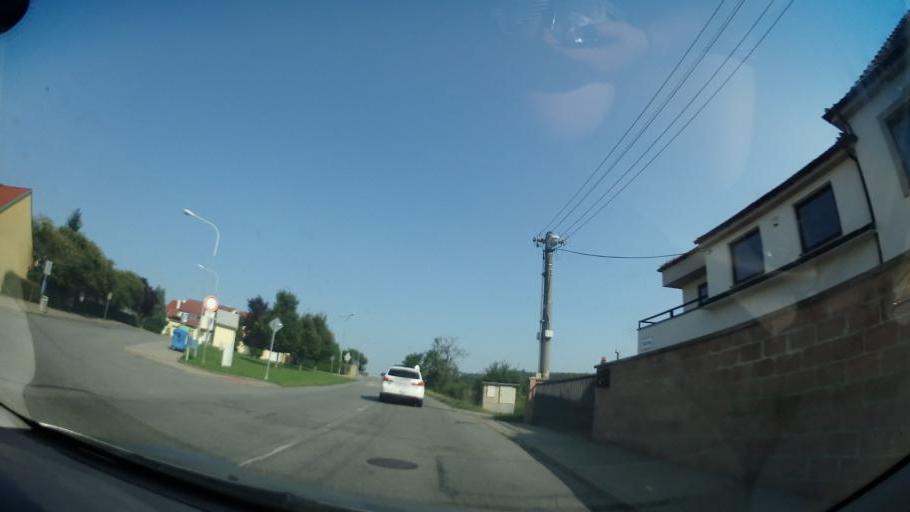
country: CZ
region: South Moravian
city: Kurim
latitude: 49.2387
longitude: 16.5305
